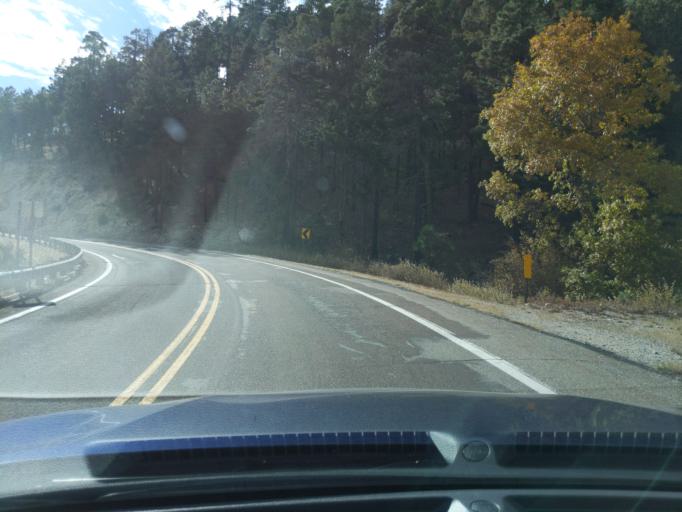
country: US
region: Arizona
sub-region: Pima County
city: Tanque Verde
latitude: 32.4111
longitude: -110.7227
